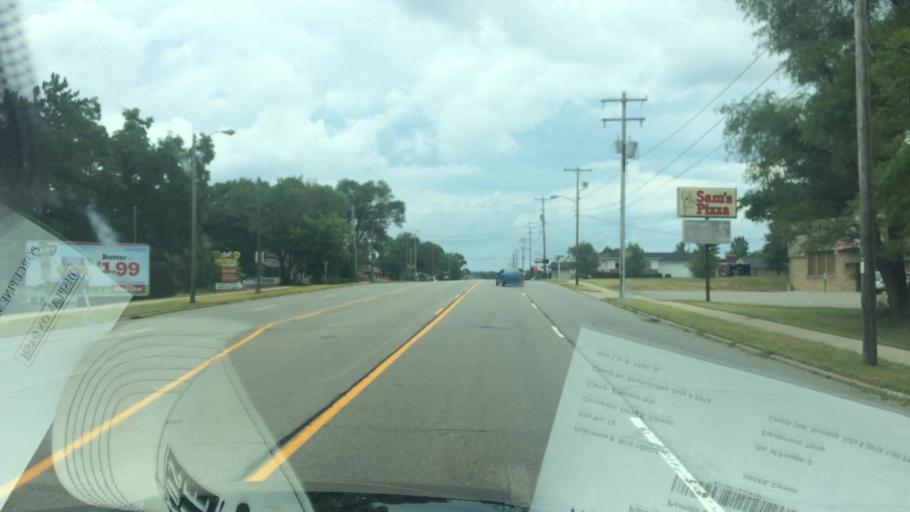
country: US
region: Wisconsin
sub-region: Marathon County
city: Schofield
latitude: 44.9034
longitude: -89.6072
